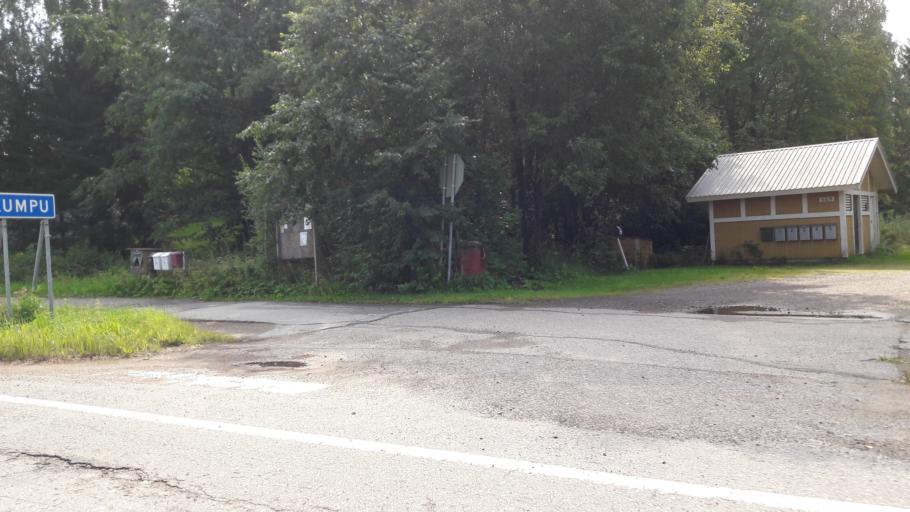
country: FI
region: North Karelia
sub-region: Joensuu
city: Pyhaeselkae
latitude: 62.5193
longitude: 29.8687
